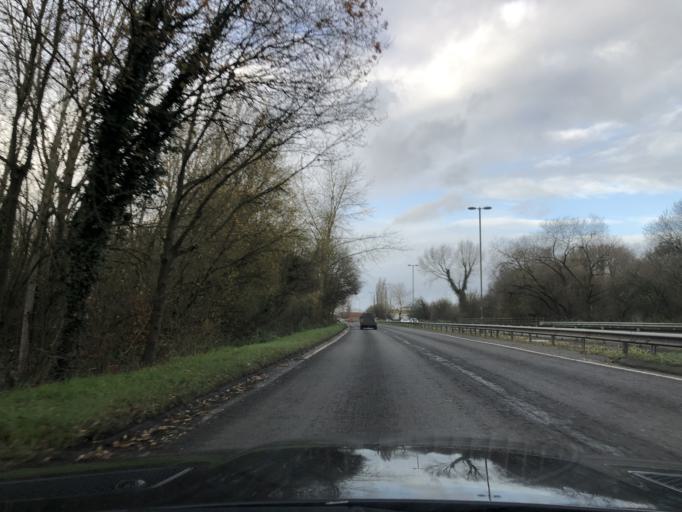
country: GB
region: England
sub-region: Surrey
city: Frimley
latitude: 51.3261
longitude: -0.7667
